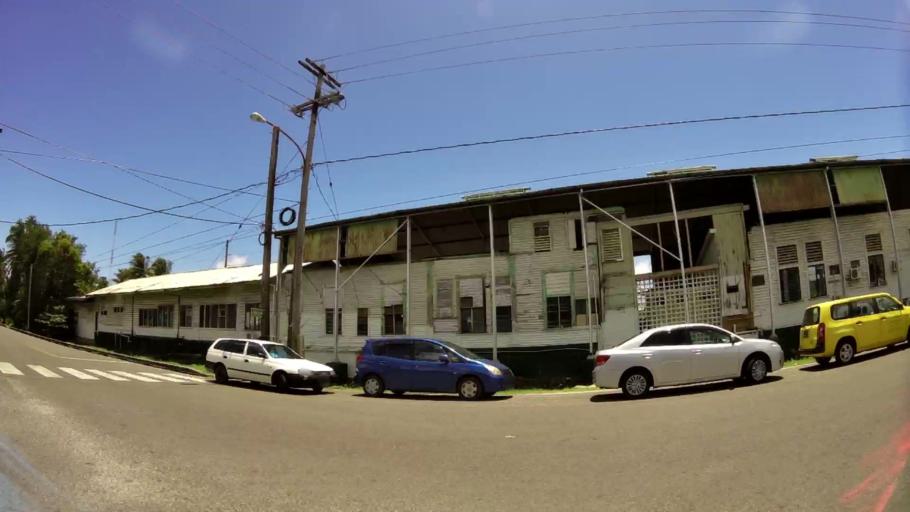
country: GY
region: Demerara-Mahaica
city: Georgetown
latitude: 6.8195
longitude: -58.1618
